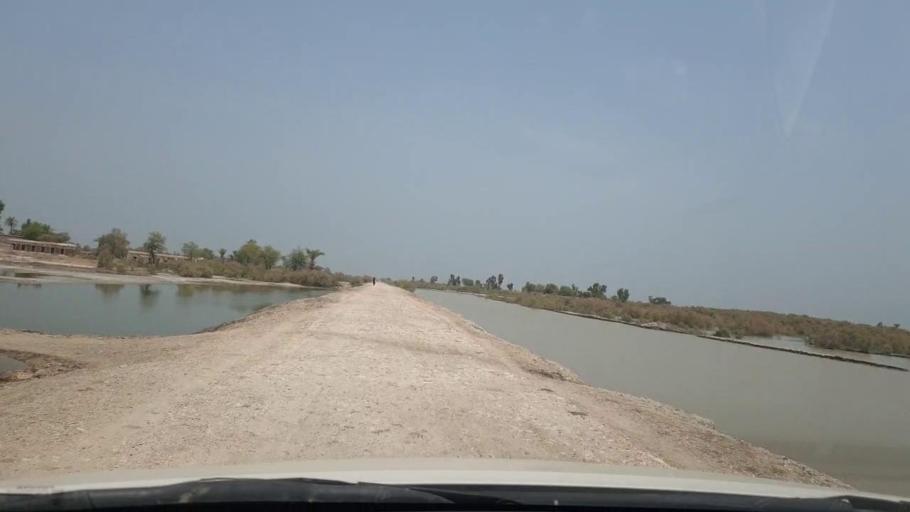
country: PK
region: Sindh
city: Rustam jo Goth
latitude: 28.0552
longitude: 68.8160
